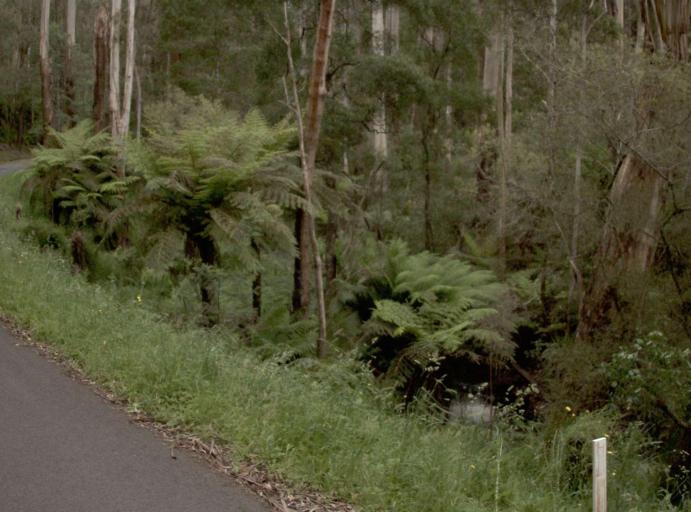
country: AU
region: Victoria
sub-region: Baw Baw
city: Warragul
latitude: -37.8911
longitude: 146.0891
